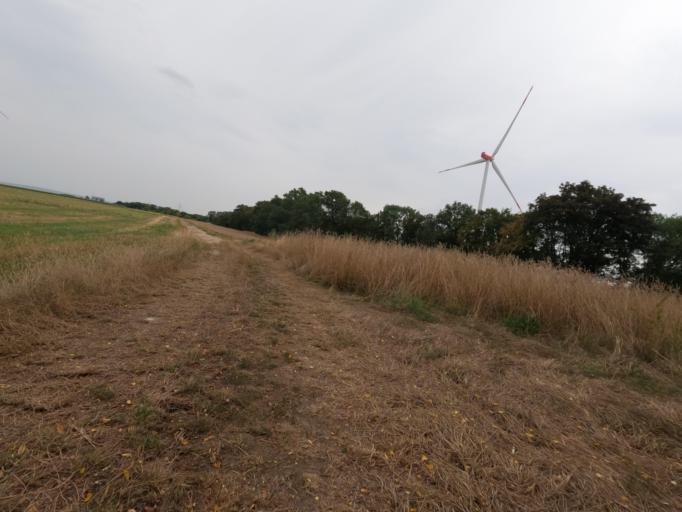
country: DE
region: North Rhine-Westphalia
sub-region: Regierungsbezirk Koln
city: Linnich
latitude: 50.9423
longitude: 6.2707
